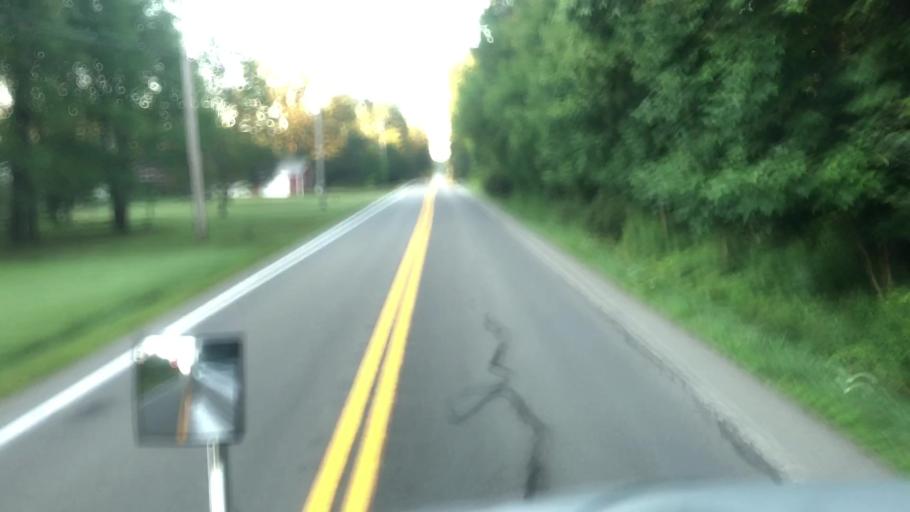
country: US
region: Pennsylvania
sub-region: Crawford County
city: Titusville
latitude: 41.5795
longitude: -79.6098
